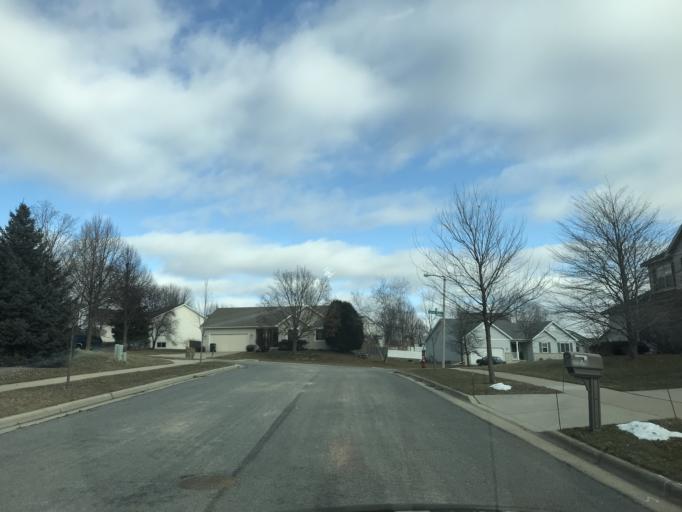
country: US
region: Wisconsin
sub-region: Dane County
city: Monona
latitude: 43.1193
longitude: -89.2943
